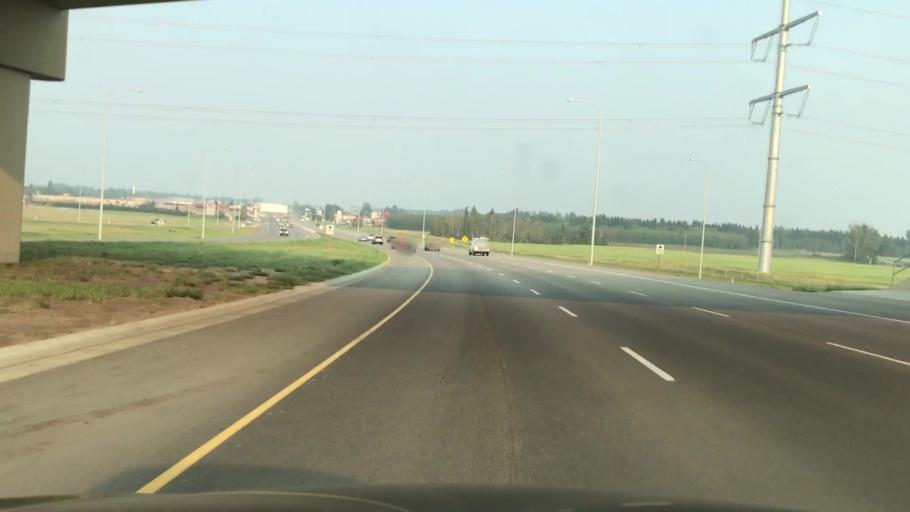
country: CA
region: Alberta
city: Sherwood Park
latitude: 53.5122
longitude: -113.3410
